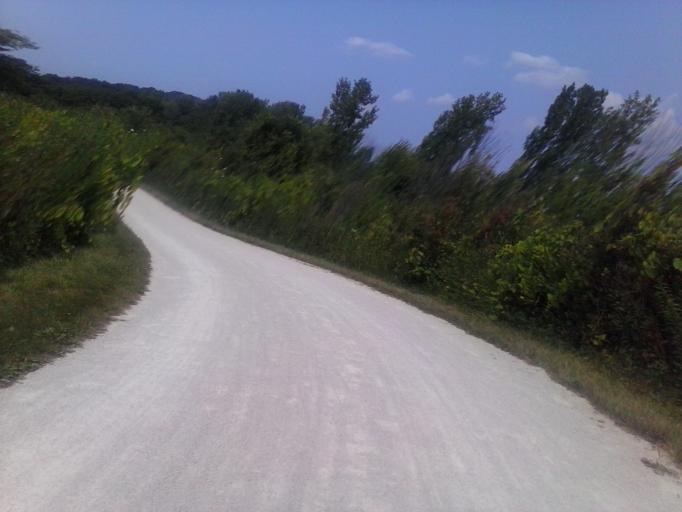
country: US
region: Illinois
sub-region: DuPage County
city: Naperville
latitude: 41.8225
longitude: -88.1242
